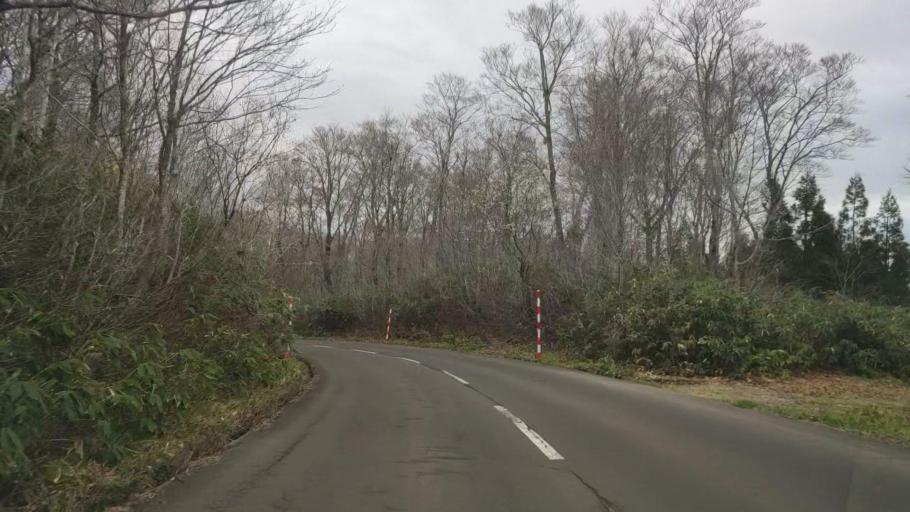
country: JP
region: Akita
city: Hanawa
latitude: 40.4184
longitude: 140.8208
